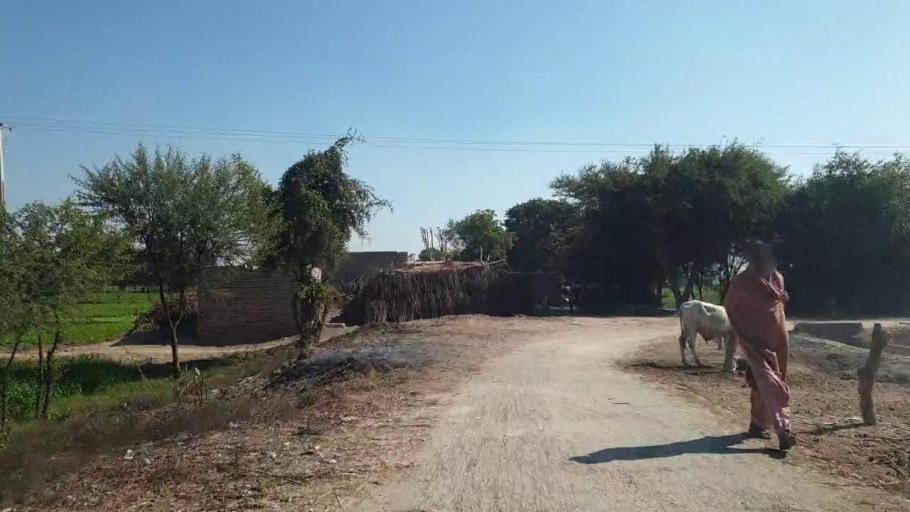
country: PK
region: Sindh
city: Shahpur Chakar
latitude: 26.1277
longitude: 68.6406
